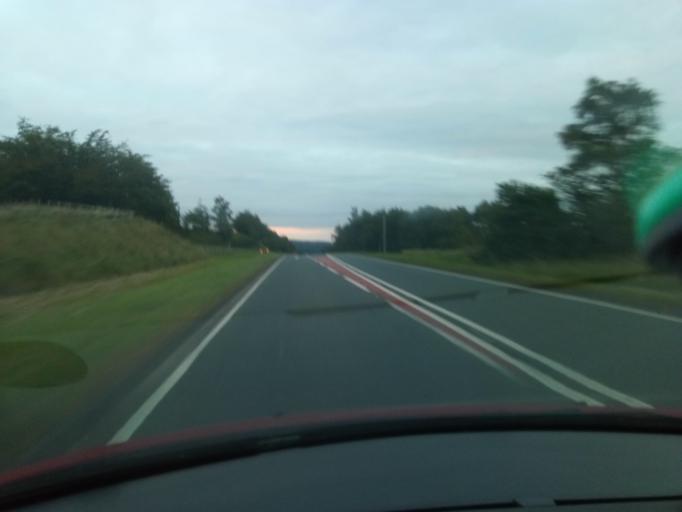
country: GB
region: England
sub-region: Northumberland
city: Bardon Mill
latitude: 54.9722
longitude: -2.3874
